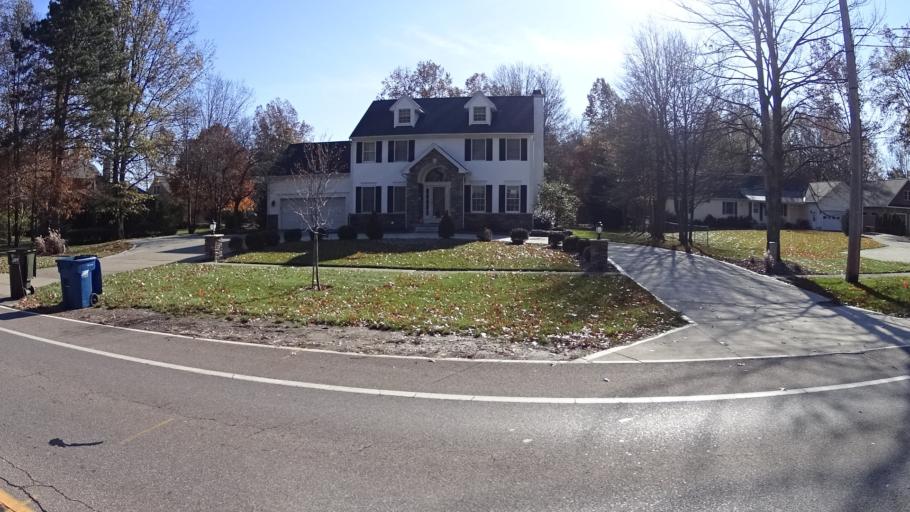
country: US
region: Ohio
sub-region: Lorain County
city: Avon Lake
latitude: 41.4930
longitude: -81.9955
